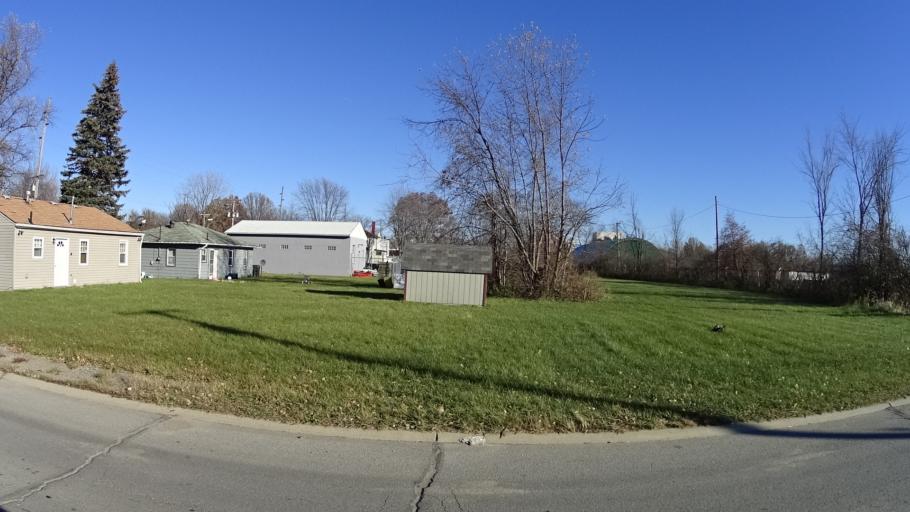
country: US
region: Ohio
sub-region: Lorain County
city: Elyria
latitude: 41.3630
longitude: -82.1237
